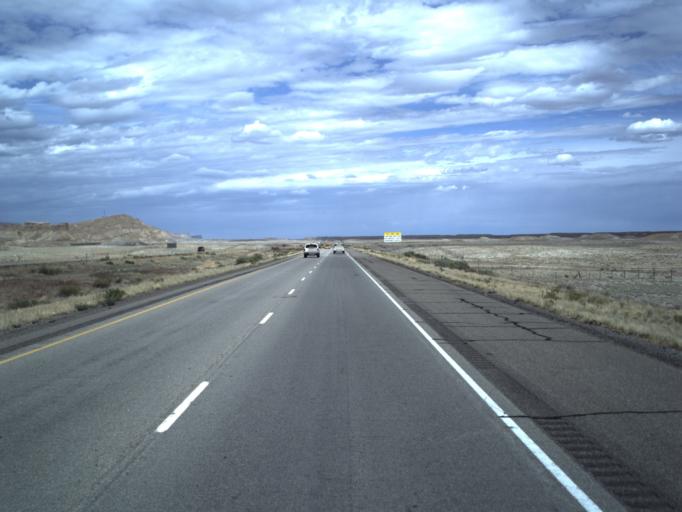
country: US
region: Utah
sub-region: Grand County
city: Moab
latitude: 38.9238
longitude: -109.9167
